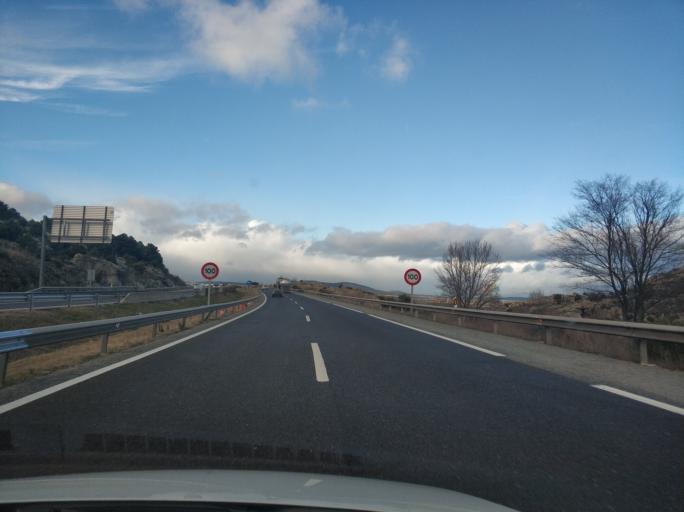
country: ES
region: Madrid
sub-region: Provincia de Madrid
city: La Cabrera
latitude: 40.8867
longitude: -3.5987
